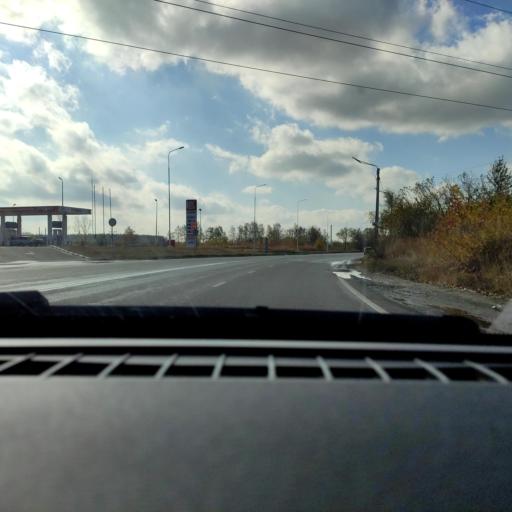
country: RU
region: Voronezj
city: Maslovka
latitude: 51.6281
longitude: 39.2861
